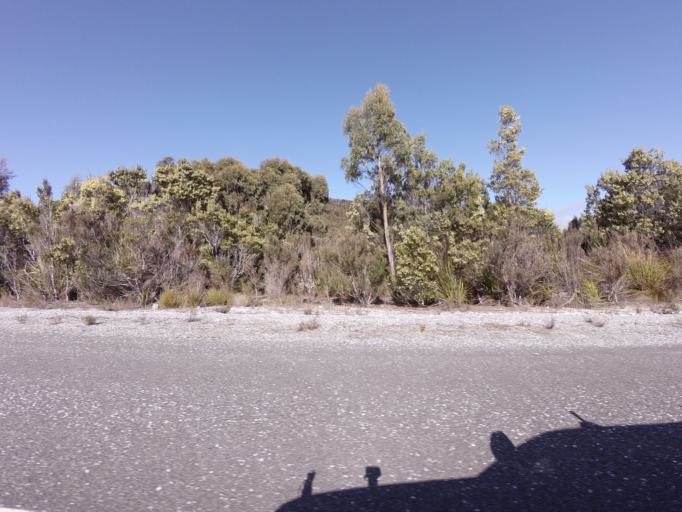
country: AU
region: Tasmania
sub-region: West Coast
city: Queenstown
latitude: -42.7917
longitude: 146.0634
